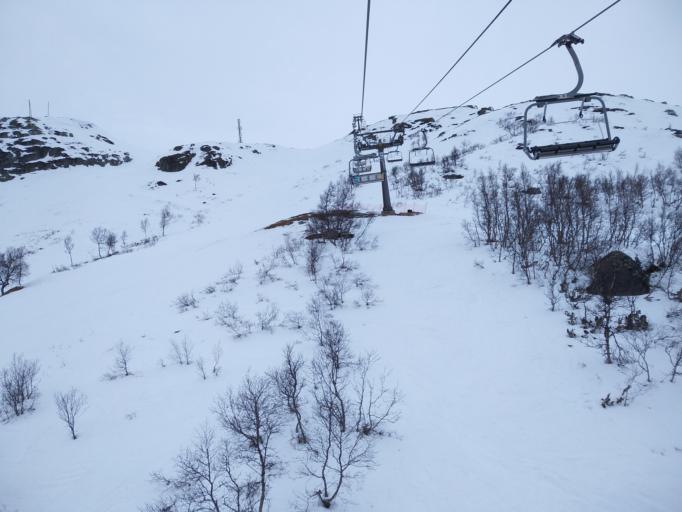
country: NO
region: Aust-Agder
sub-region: Bykle
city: Hovden
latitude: 59.5762
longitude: 7.3377
